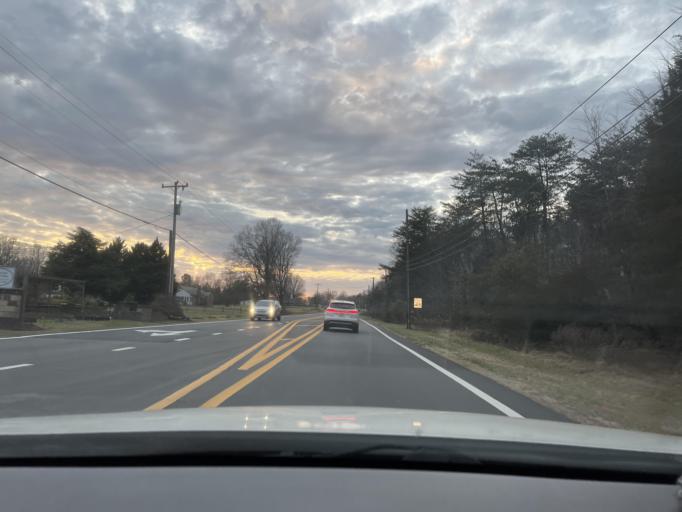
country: US
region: North Carolina
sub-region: Guilford County
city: Gibsonville
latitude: 36.0773
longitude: -79.5650
